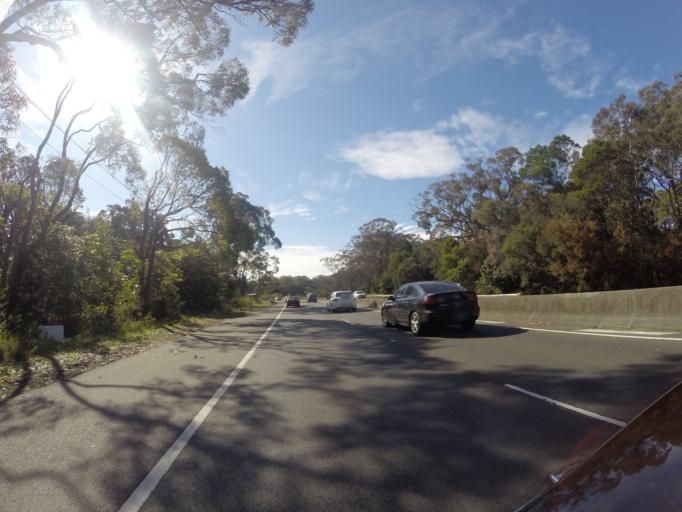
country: AU
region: New South Wales
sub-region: Sutherland Shire
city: Loftus
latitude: -34.0505
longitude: 151.0510
